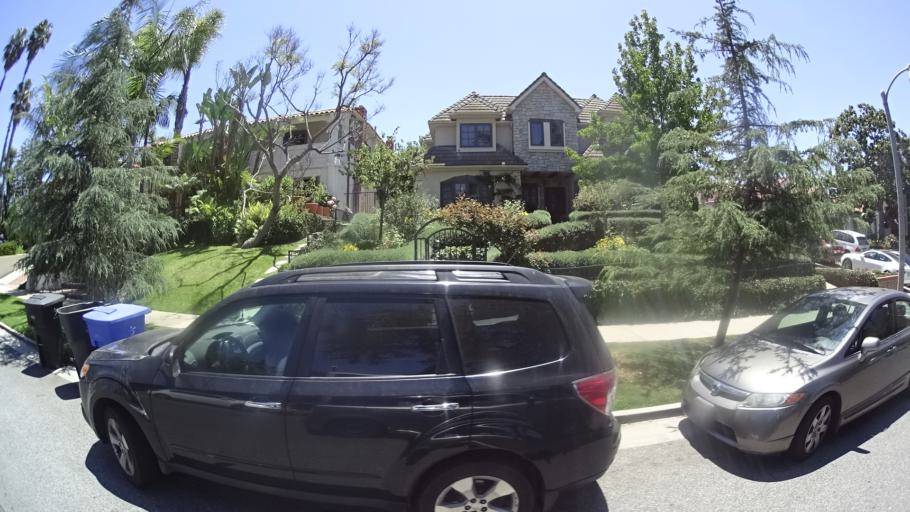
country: US
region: California
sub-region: Los Angeles County
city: Santa Monica
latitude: 34.0462
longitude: -118.4911
